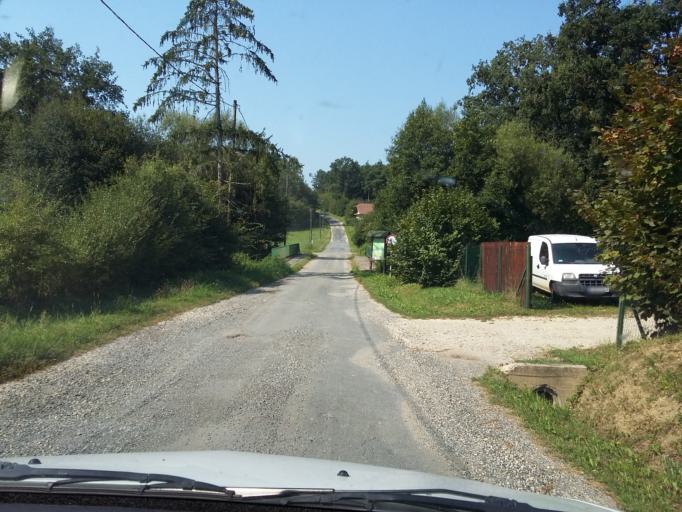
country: SI
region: Hodos-Hodos
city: Hodos
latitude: 46.8658
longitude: 16.3625
